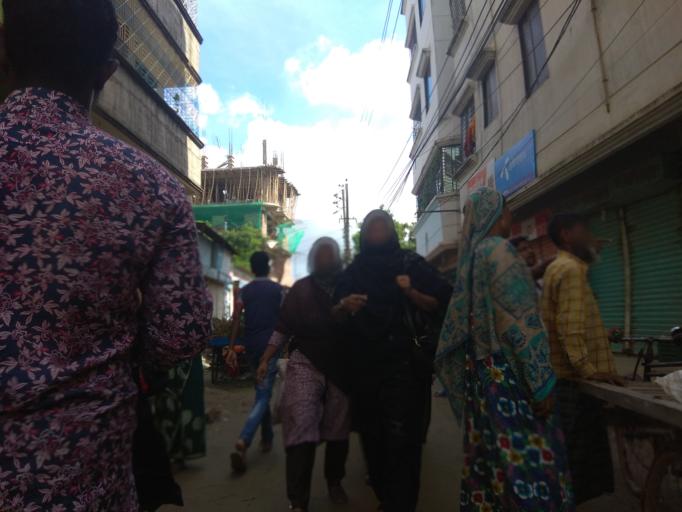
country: BD
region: Dhaka
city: Tungi
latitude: 23.8152
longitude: 90.3871
